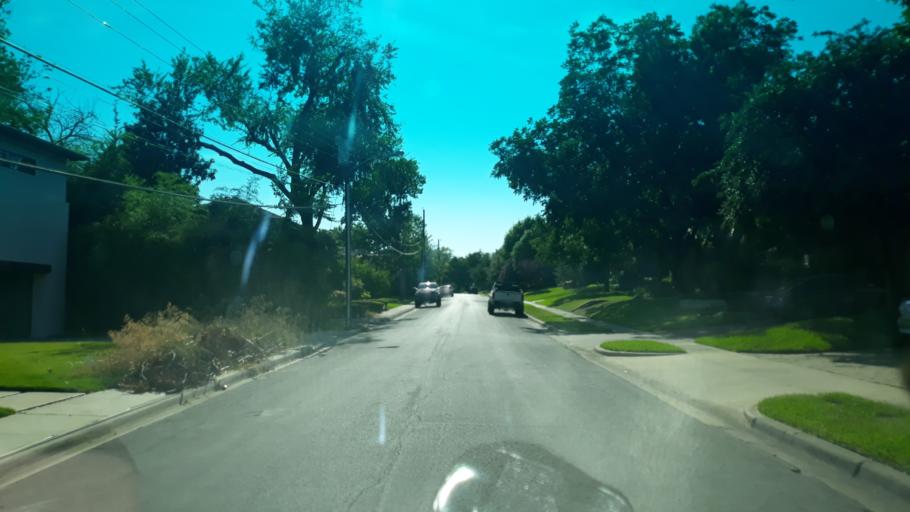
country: US
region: Texas
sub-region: Dallas County
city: Highland Park
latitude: 32.8250
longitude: -96.7455
